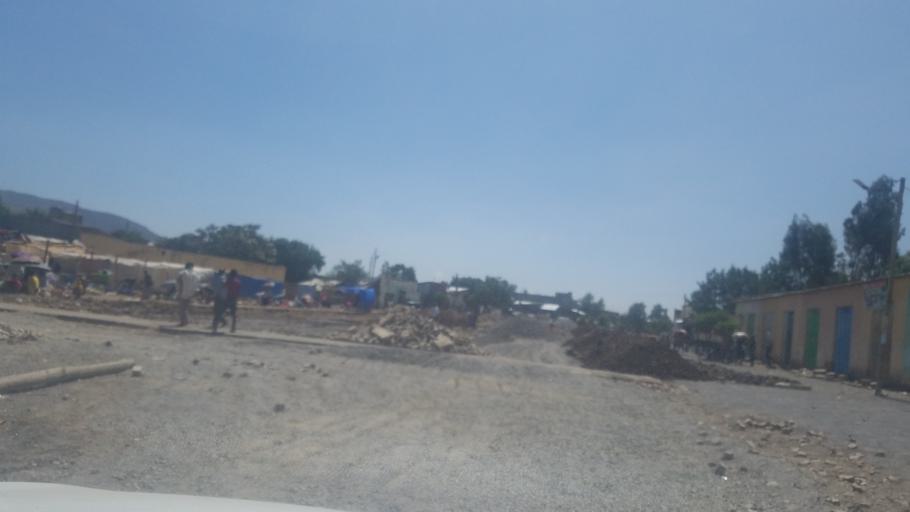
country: ET
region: Tigray
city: Mekele
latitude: 13.7947
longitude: 39.5990
